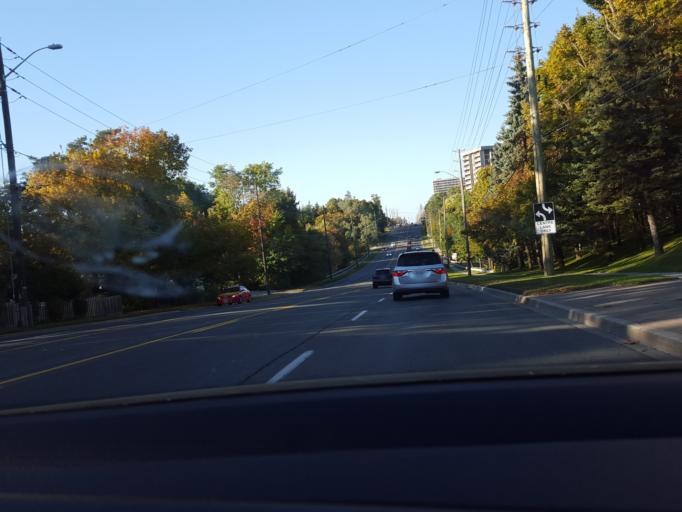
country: CA
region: Ontario
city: North York
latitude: 43.8175
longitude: -79.4247
